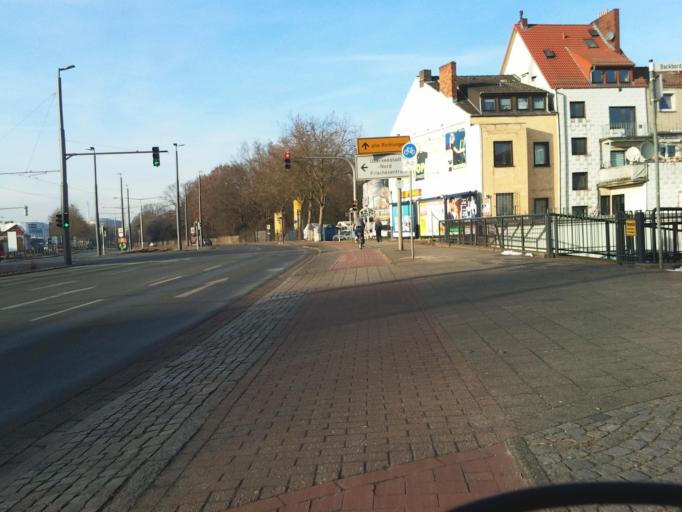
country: DE
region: Bremen
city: Bremen
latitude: 53.1010
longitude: 8.7749
